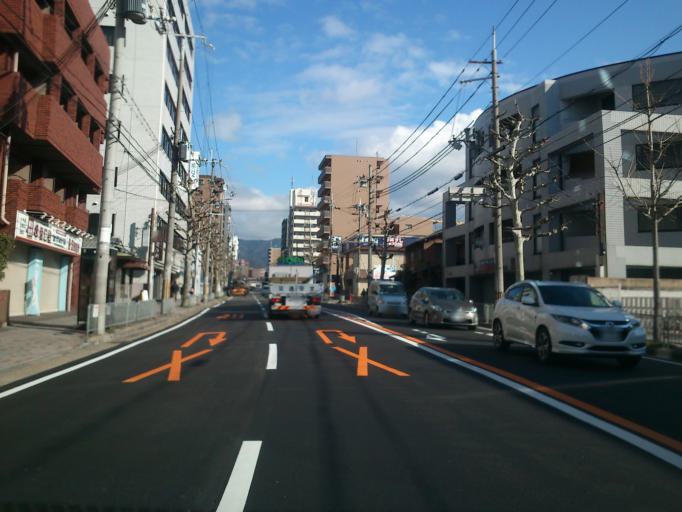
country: JP
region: Shiga Prefecture
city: Otsu-shi
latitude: 34.9741
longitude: 135.8158
